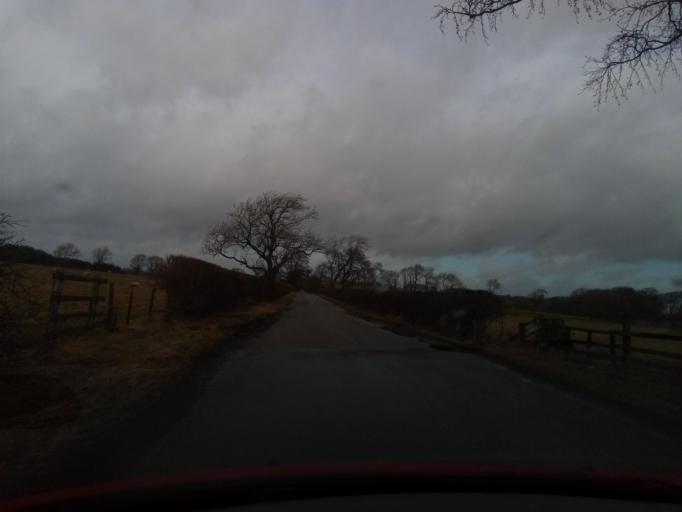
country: GB
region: England
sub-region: Northumberland
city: Rothley
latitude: 55.1790
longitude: -1.9677
